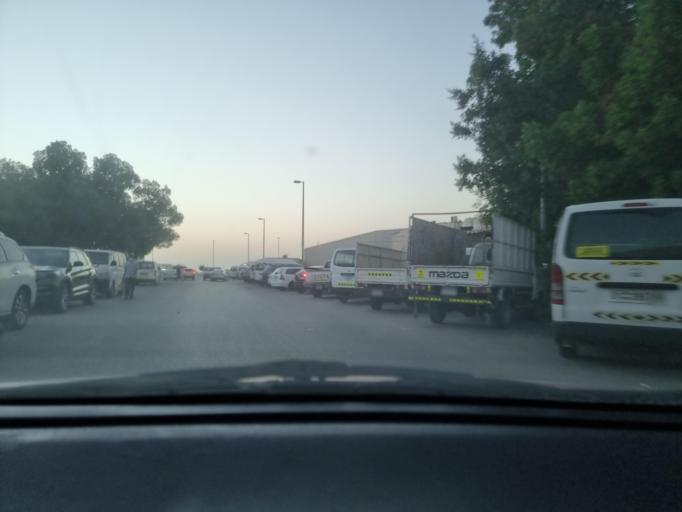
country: AE
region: Abu Dhabi
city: Abu Dhabi
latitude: 24.3512
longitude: 54.5187
